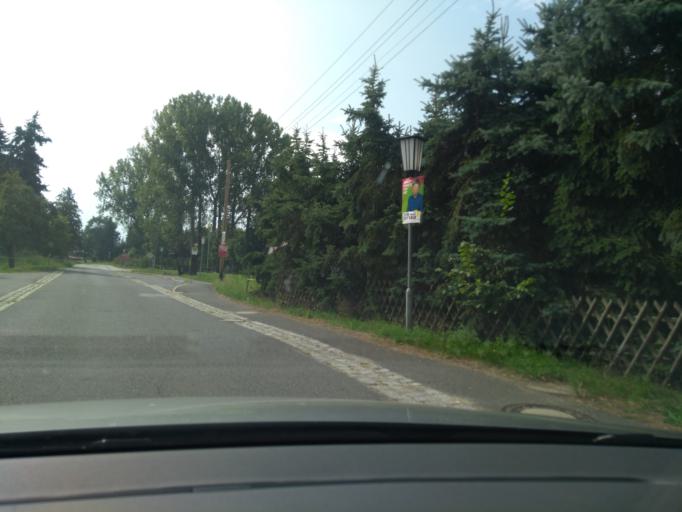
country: DE
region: Saxony
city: Markersdorf
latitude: 51.1408
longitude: 14.8754
